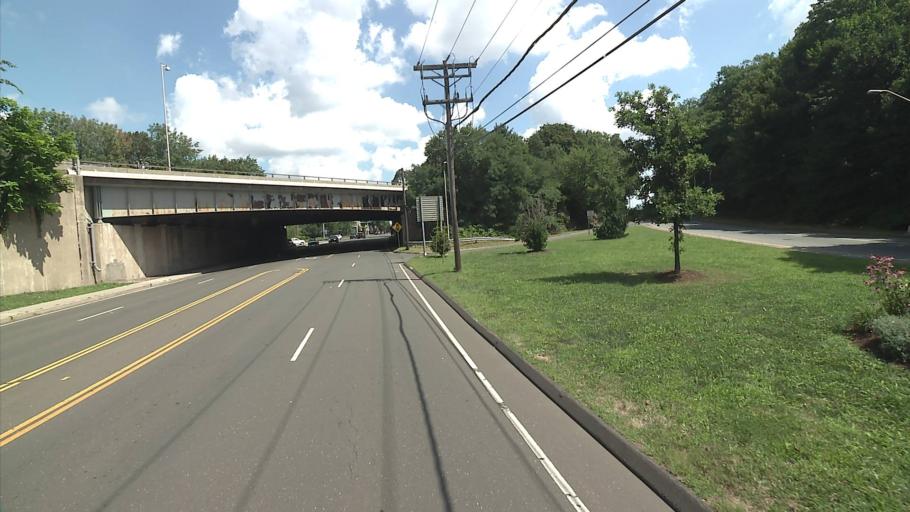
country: US
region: Connecticut
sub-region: Fairfield County
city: Darien
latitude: 41.0719
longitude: -73.4753
